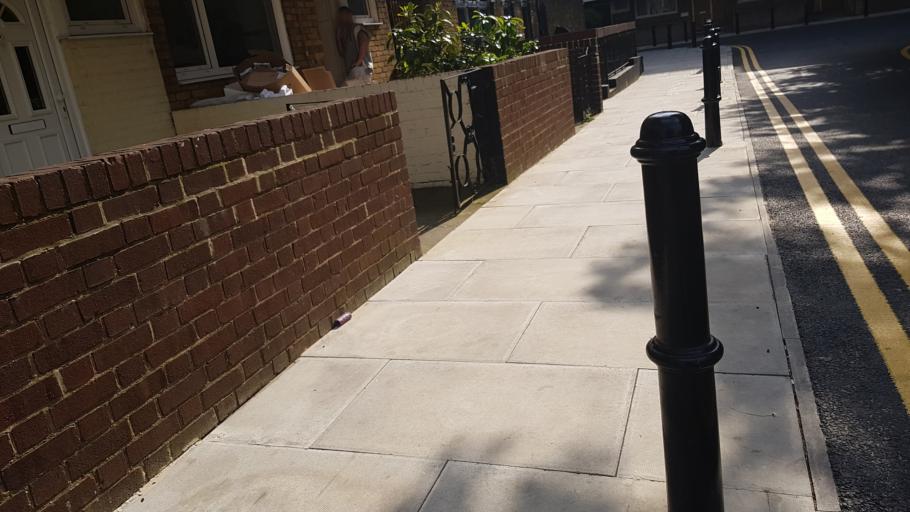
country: GB
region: England
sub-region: Greater London
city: Hackney
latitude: 51.5327
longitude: -0.0335
